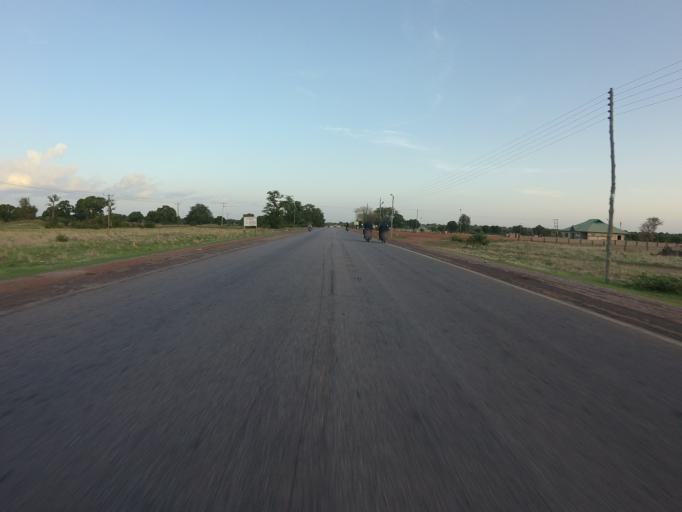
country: GH
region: Upper East
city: Navrongo
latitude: 10.9398
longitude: -1.0914
